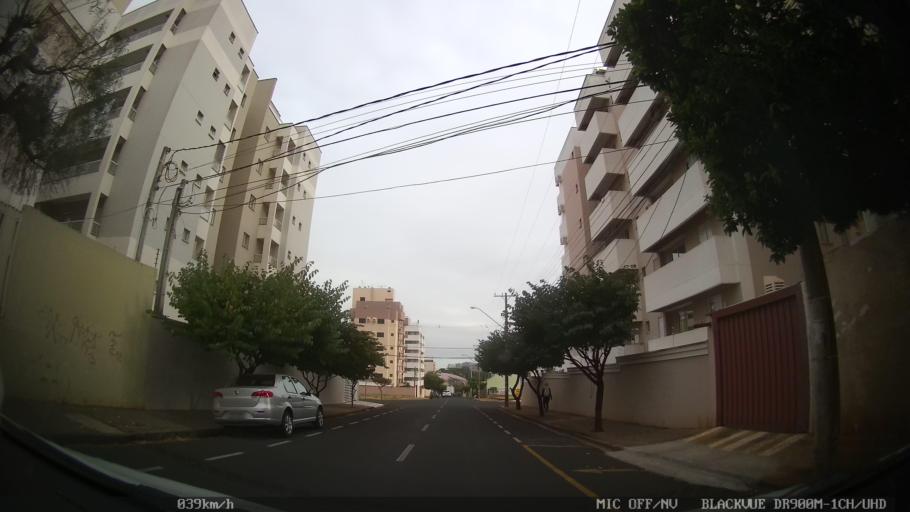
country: BR
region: Sao Paulo
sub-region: Sao Jose Do Rio Preto
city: Sao Jose do Rio Preto
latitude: -20.8361
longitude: -49.3896
